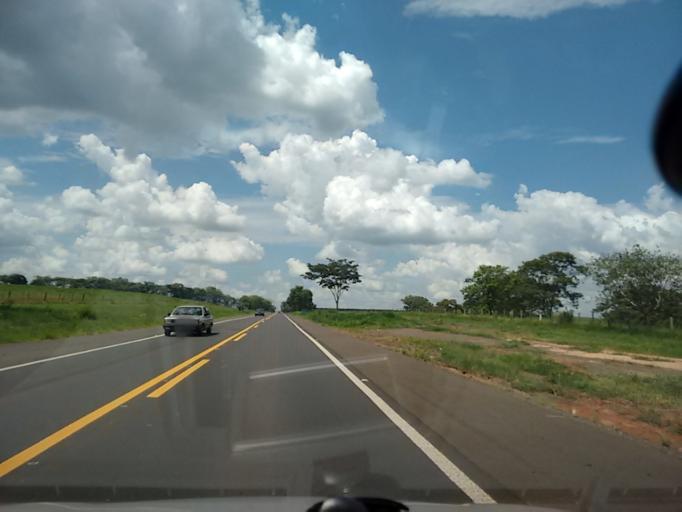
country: BR
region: Sao Paulo
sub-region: Osvaldo Cruz
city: Osvaldo Cruz
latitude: -21.8794
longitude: -50.8629
